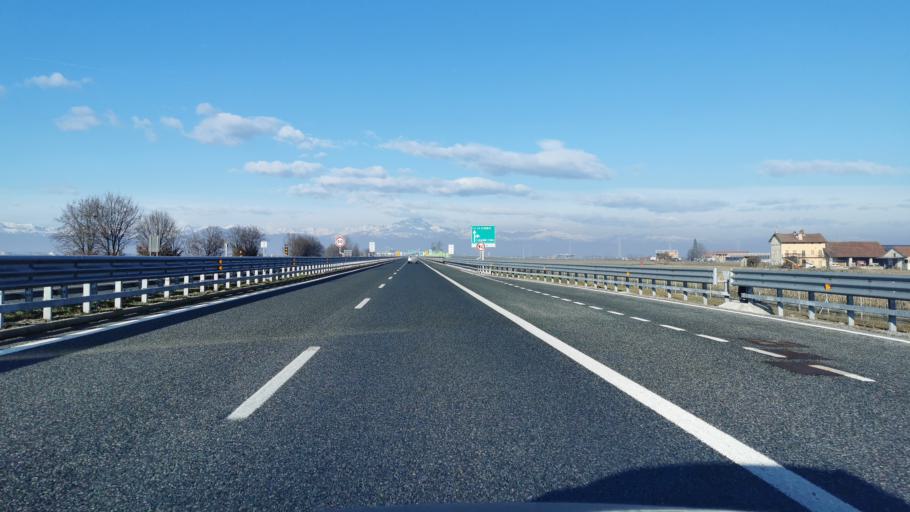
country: IT
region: Piedmont
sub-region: Provincia di Cuneo
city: Sant'Albano Stura
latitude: 44.4725
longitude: 7.7057
